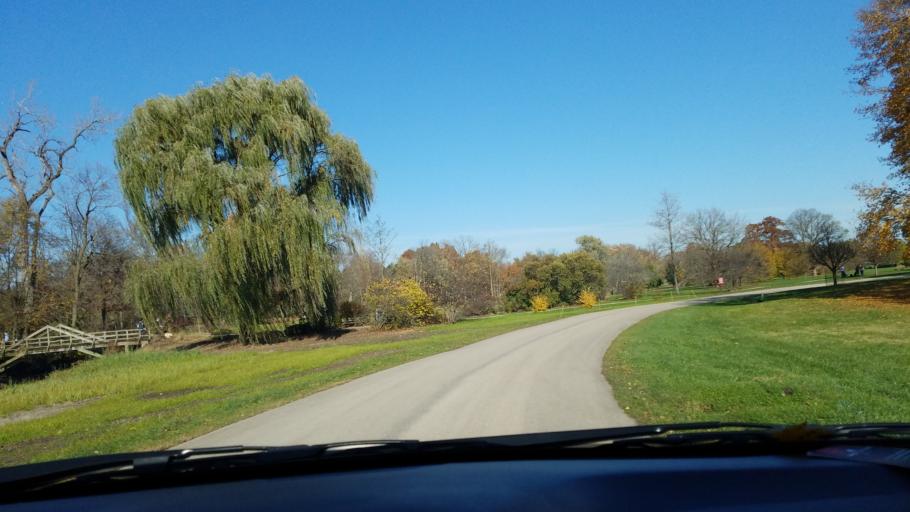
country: US
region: Illinois
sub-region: DuPage County
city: Lisle
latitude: 41.8137
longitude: -88.0782
